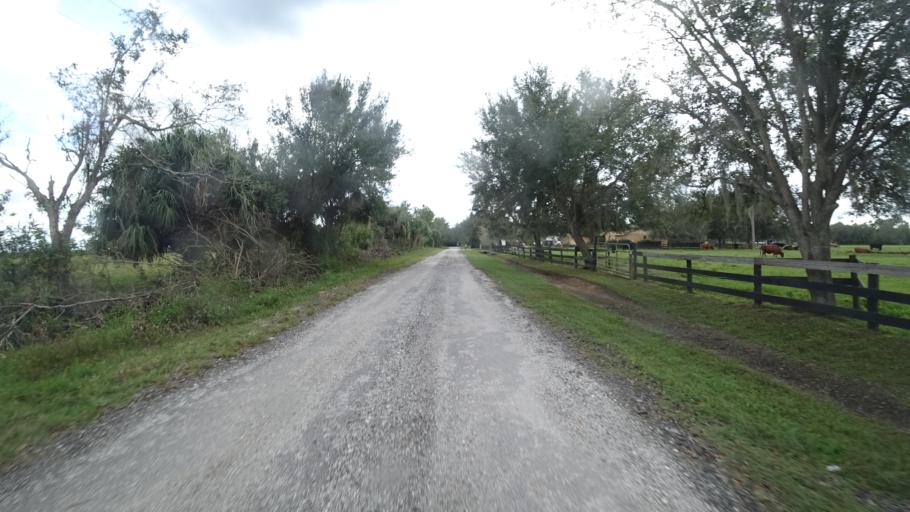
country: US
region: Florida
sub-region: Sarasota County
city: Lake Sarasota
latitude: 27.3959
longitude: -82.2664
